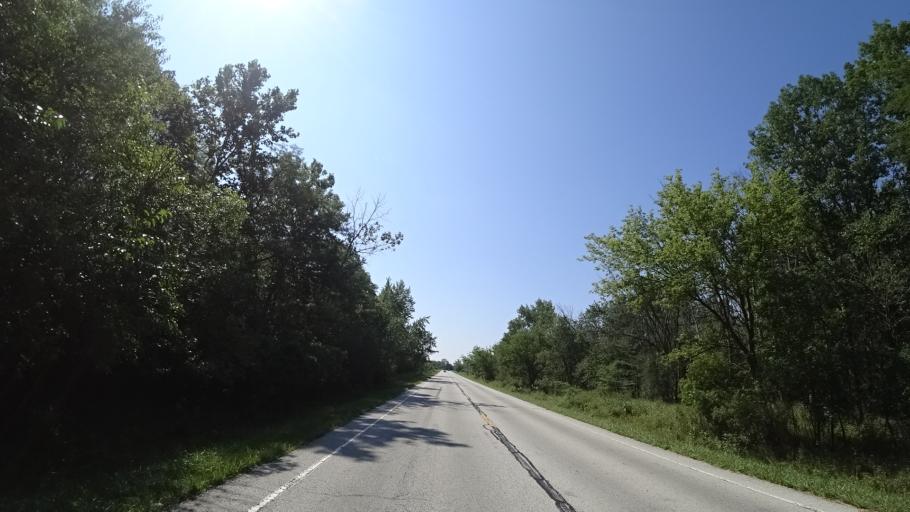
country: US
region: Illinois
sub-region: Cook County
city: Country Club Hills
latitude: 41.5346
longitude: -87.7517
